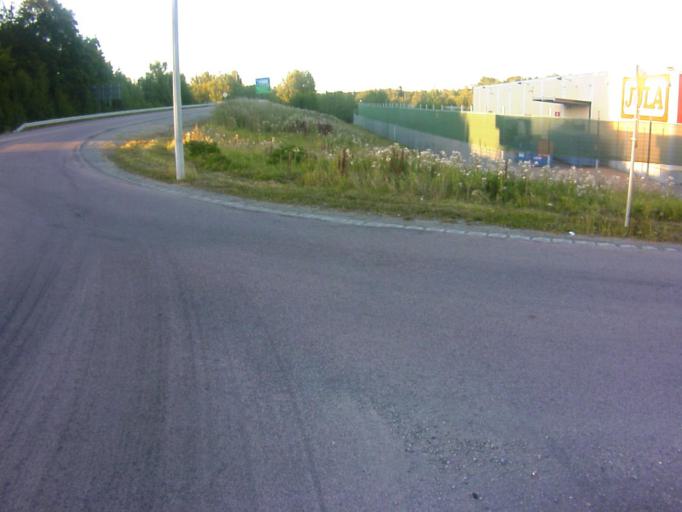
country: SE
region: Soedermanland
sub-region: Eskilstuna Kommun
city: Hallbybrunn
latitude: 59.4037
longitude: 16.4207
